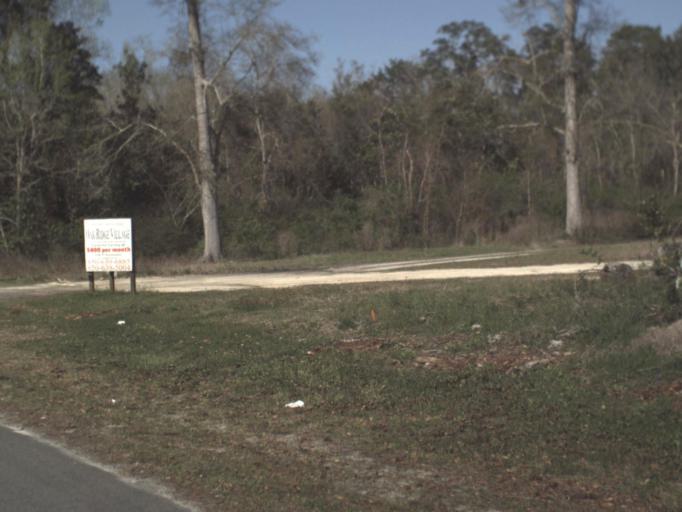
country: US
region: Florida
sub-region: Gulf County
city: Wewahitchka
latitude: 30.1007
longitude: -85.2006
